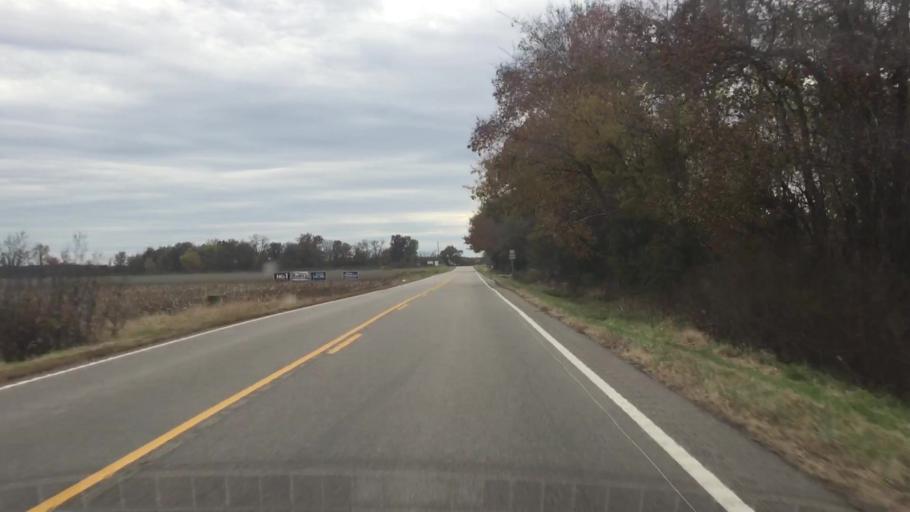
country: US
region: Missouri
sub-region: Callaway County
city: Holts Summit
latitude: 38.6067
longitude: -91.9885
